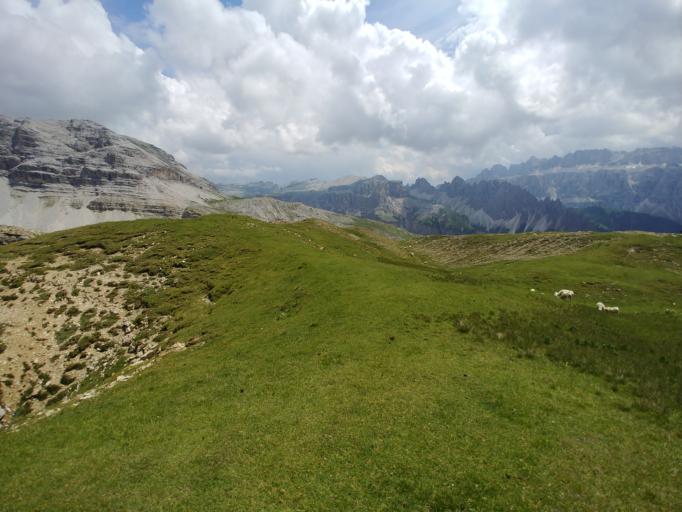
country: IT
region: Trentino-Alto Adige
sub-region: Bolzano
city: Selva
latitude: 46.5809
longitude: 11.7679
